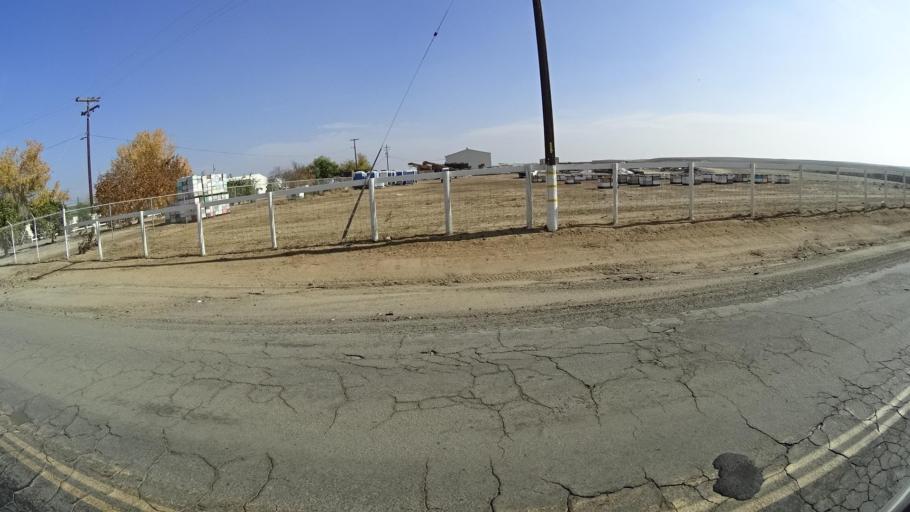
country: US
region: California
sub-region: Kern County
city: McFarland
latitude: 35.6527
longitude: -119.1337
